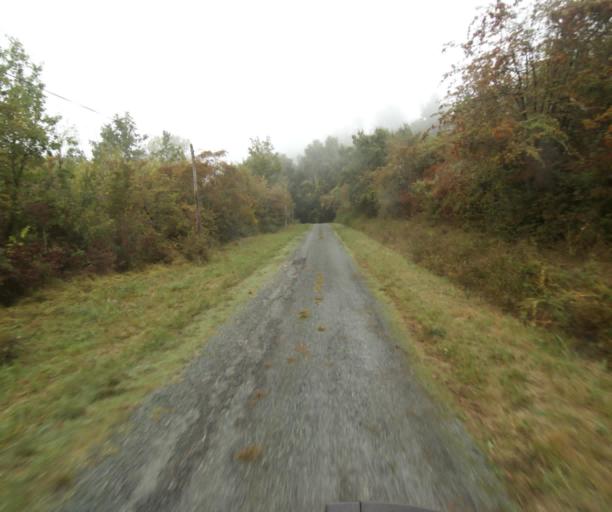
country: FR
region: Midi-Pyrenees
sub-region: Departement du Tarn-et-Garonne
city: Nohic
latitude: 43.8968
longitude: 1.4749
